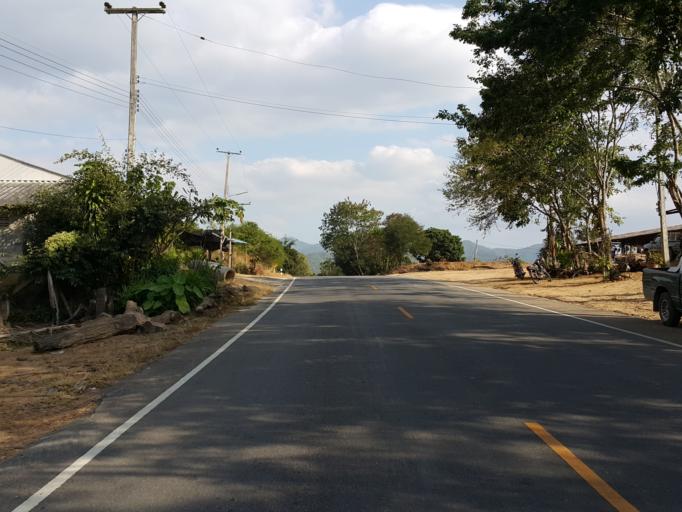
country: TH
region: Lamphun
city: Ban Hong
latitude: 18.2608
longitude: 98.9447
